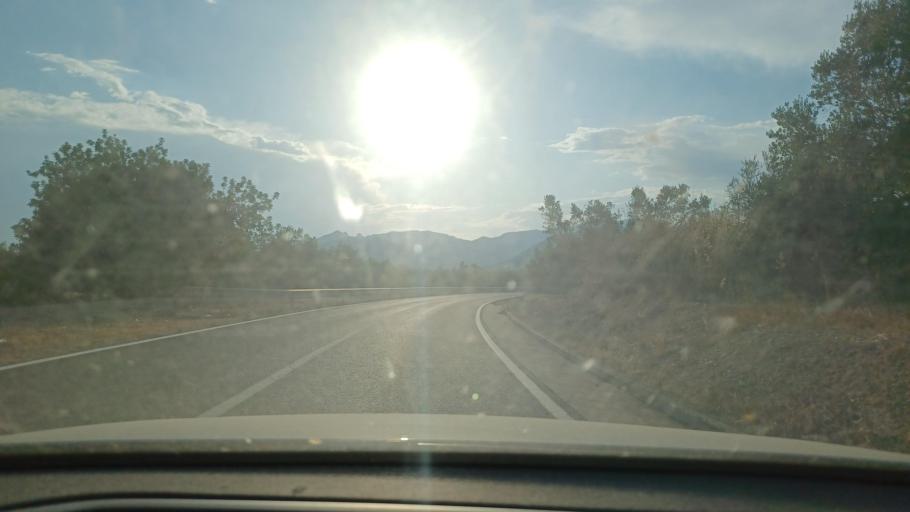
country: ES
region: Catalonia
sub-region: Provincia de Tarragona
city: Mas de Barberans
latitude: 40.7118
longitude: 0.4061
